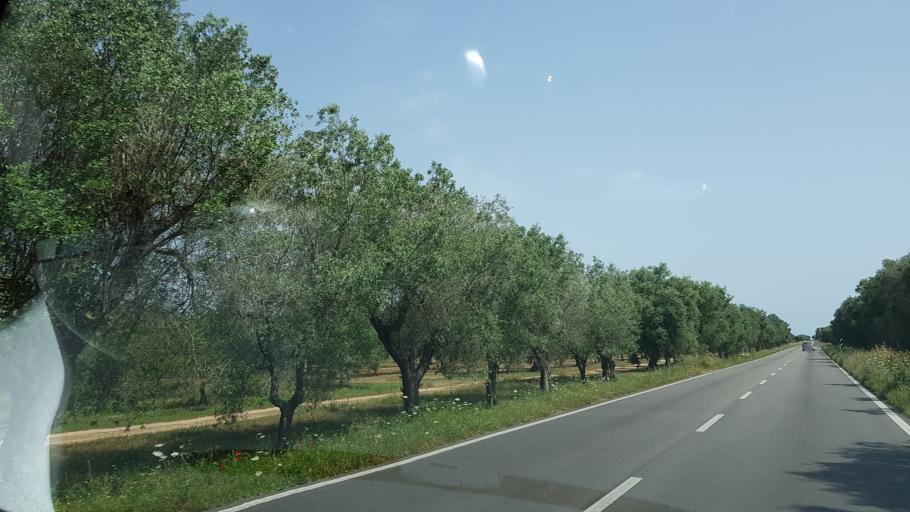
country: IT
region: Apulia
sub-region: Provincia di Brindisi
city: San Pancrazio Salentino
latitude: 40.3601
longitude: 17.8428
